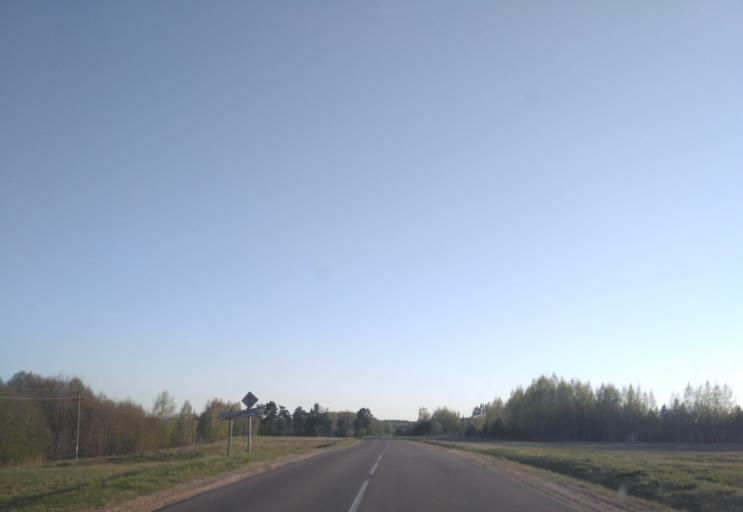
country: BY
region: Minsk
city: Radashkovichy
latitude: 54.1465
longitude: 27.2140
